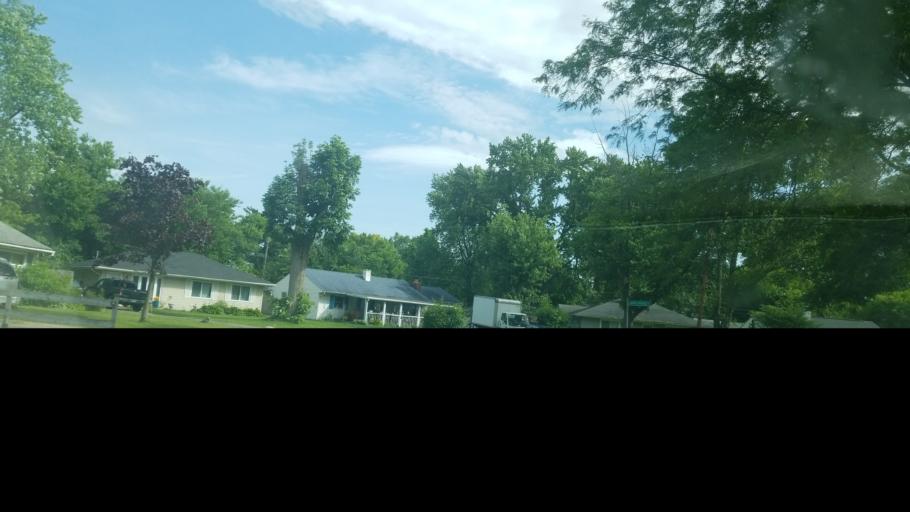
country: US
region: Ohio
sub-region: Franklin County
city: Minerva Park
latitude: 40.0410
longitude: -82.9752
